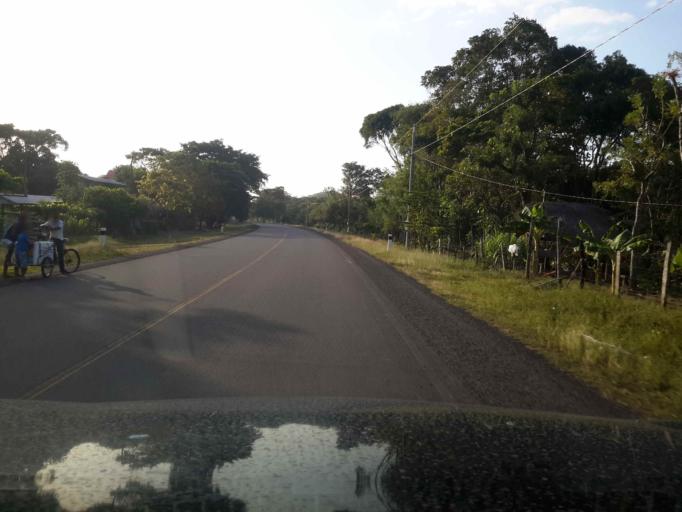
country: NI
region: Rio San Juan
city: San Miguelito
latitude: 11.3951
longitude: -84.8058
